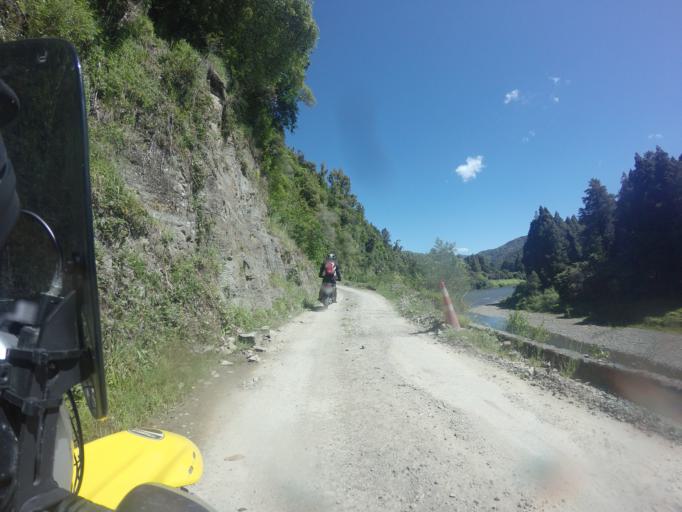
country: NZ
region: Bay of Plenty
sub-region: Opotiki District
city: Opotiki
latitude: -38.2954
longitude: 177.3383
